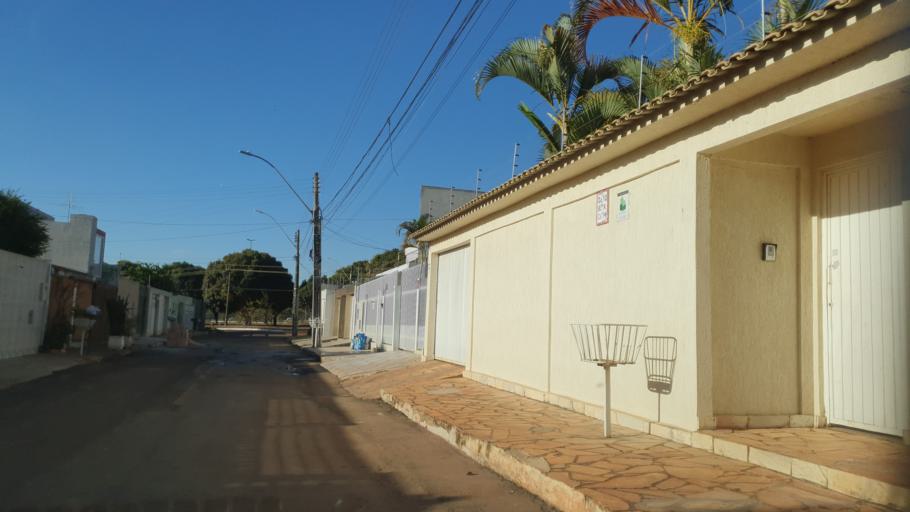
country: BR
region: Federal District
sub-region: Brasilia
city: Brasilia
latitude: -15.7815
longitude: -47.9314
